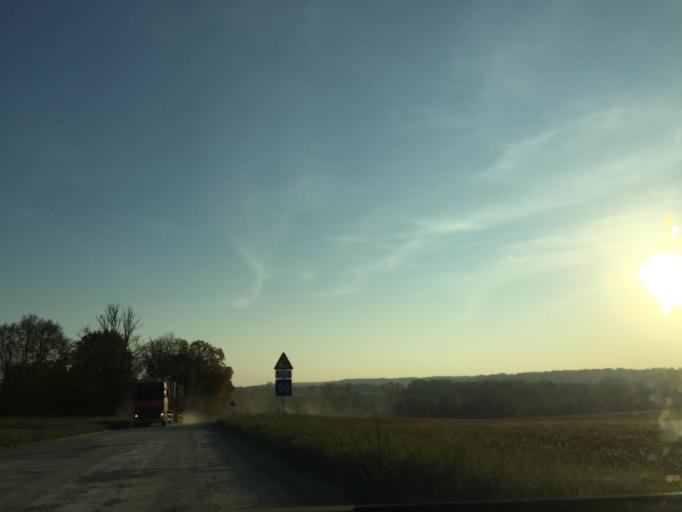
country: LV
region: Vainode
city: Vainode
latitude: 56.5313
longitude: 21.8298
